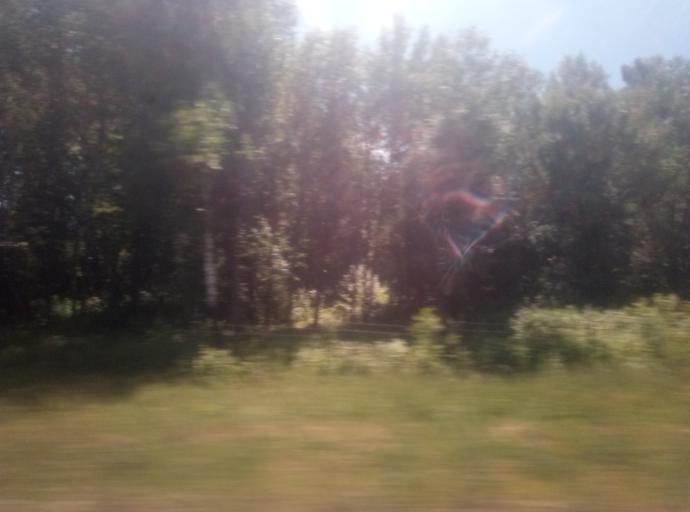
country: RU
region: Tula
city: Kireyevsk
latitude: 53.9319
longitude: 37.9386
